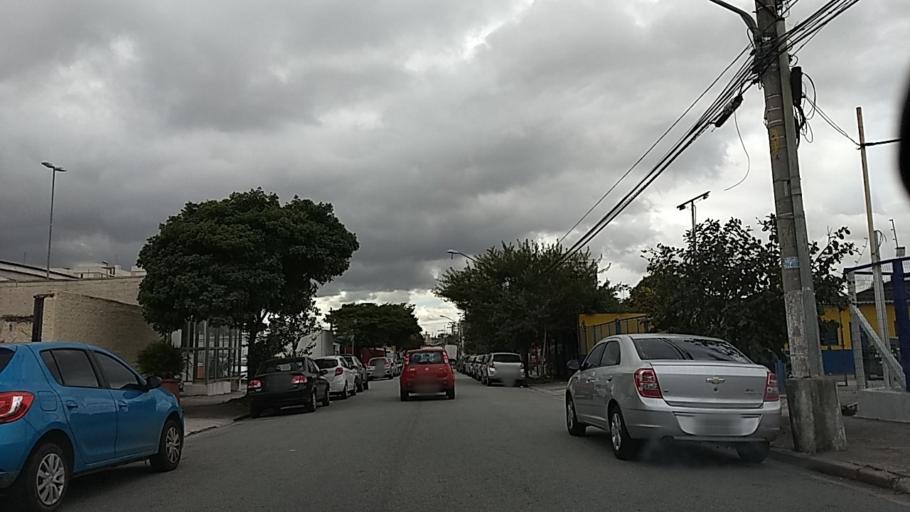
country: BR
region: Sao Paulo
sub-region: Sao Paulo
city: Sao Paulo
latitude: -23.5202
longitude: -46.6130
